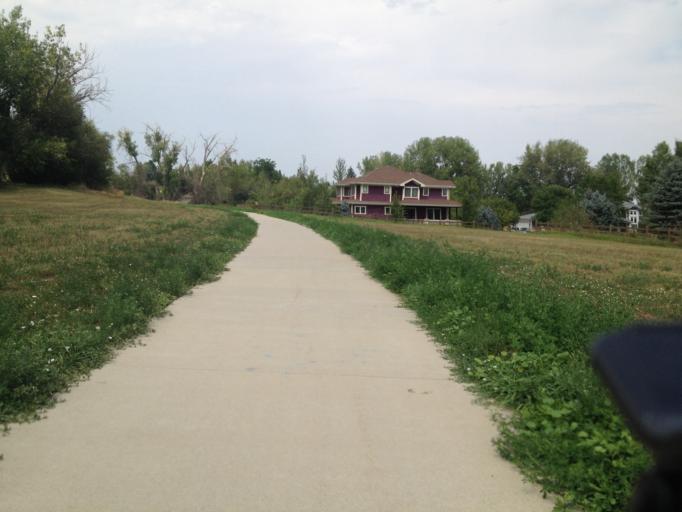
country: US
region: Colorado
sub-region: Boulder County
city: Louisville
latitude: 39.9783
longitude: -105.1466
